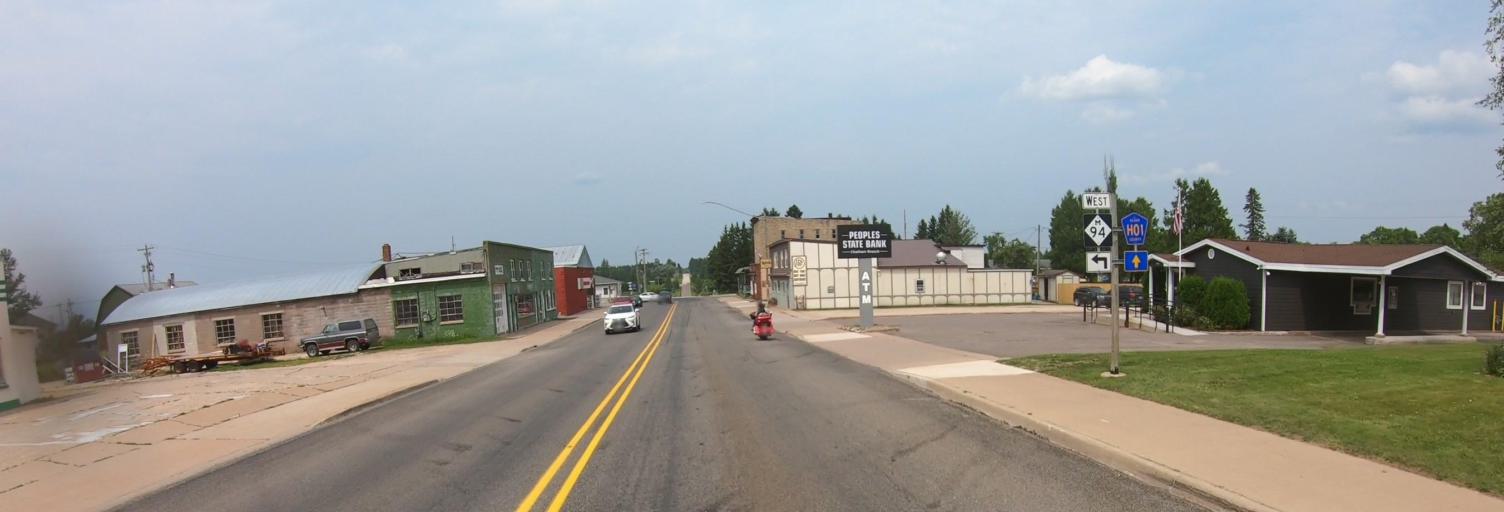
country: US
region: Michigan
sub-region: Alger County
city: Munising
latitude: 46.3463
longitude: -86.9288
